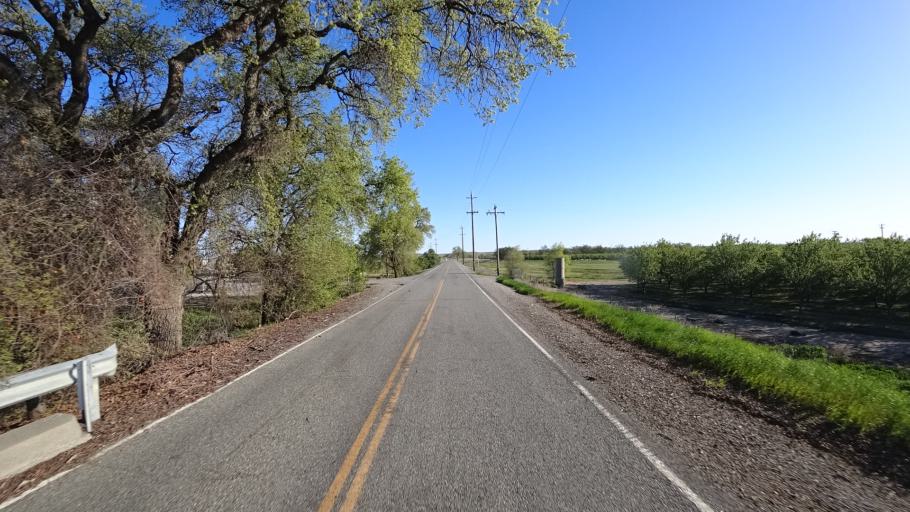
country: US
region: California
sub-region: Glenn County
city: Orland
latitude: 39.8096
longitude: -122.3302
